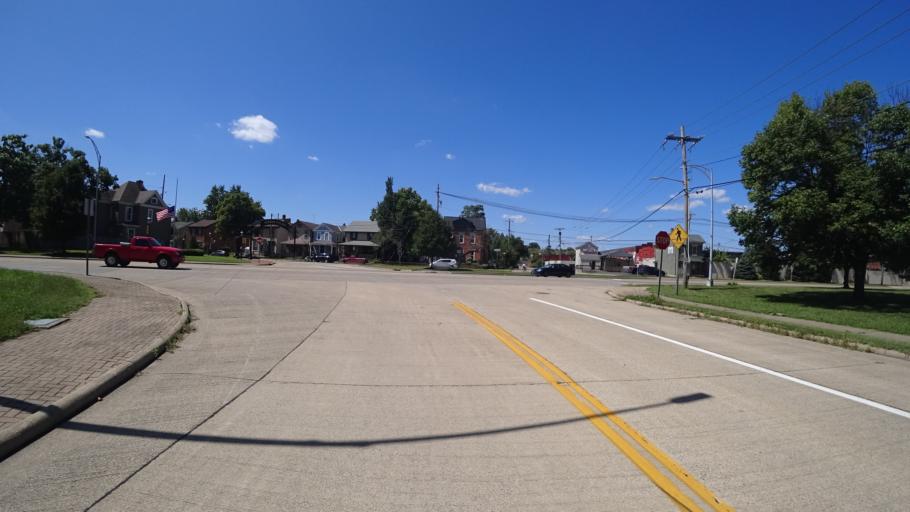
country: US
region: Ohio
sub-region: Butler County
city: Hamilton
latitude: 39.4049
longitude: -84.5569
